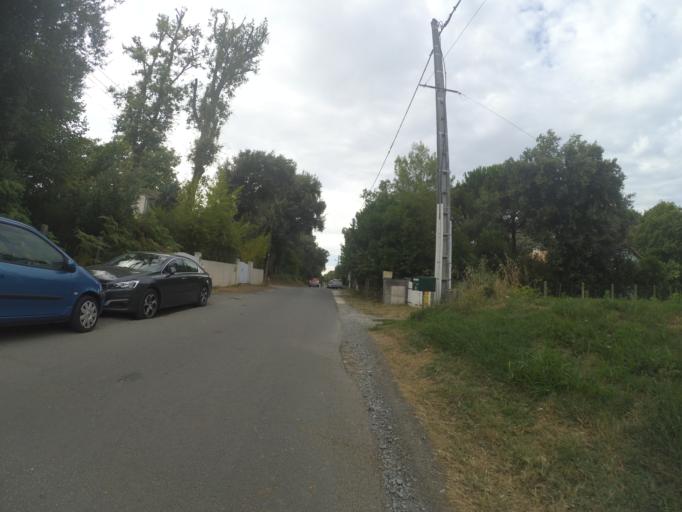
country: FR
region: Poitou-Charentes
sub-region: Departement de la Charente-Maritime
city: Meschers-sur-Gironde
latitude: 45.5671
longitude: -0.9625
